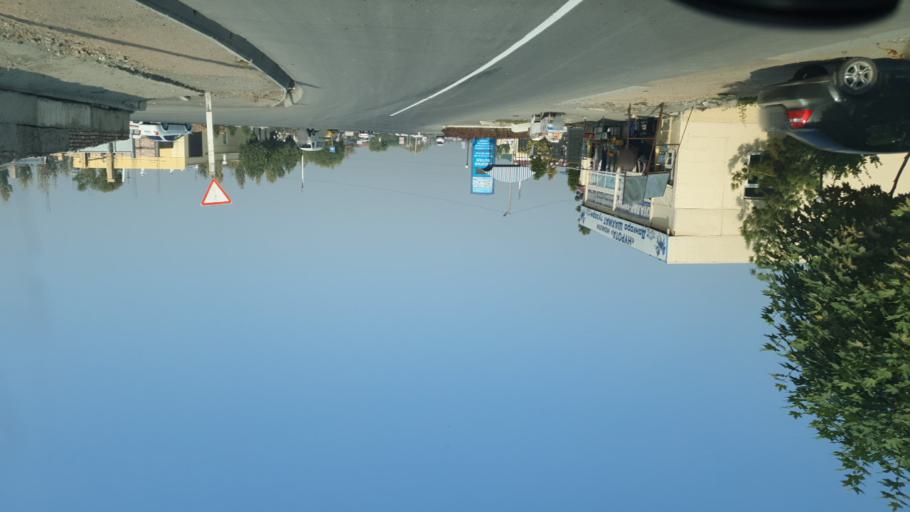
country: UZ
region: Fergana
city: Qo`qon
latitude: 40.5875
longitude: 70.9050
